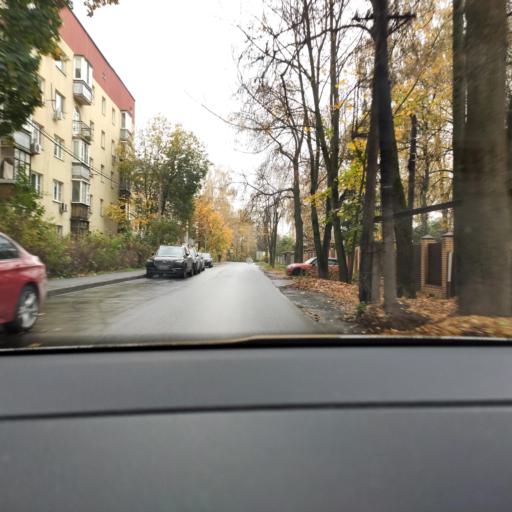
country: RU
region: Moskovskaya
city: Druzhba
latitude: 55.8870
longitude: 37.7537
